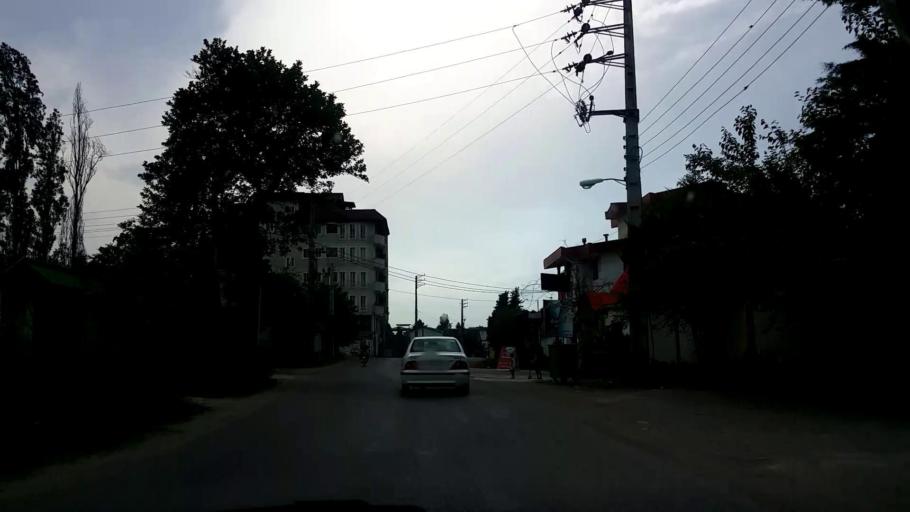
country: IR
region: Mazandaran
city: Chalus
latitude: 36.6859
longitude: 51.4138
